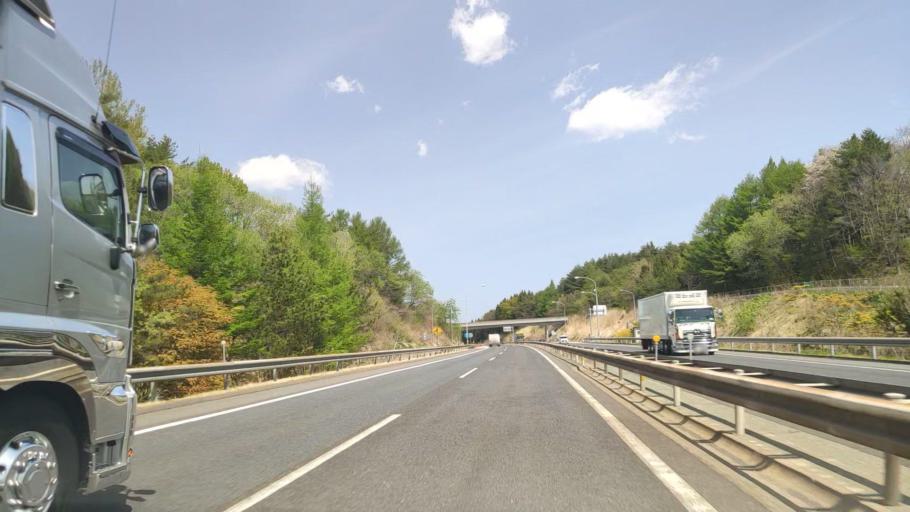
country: JP
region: Aomori
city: Hachinohe
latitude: 40.4077
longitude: 141.4437
